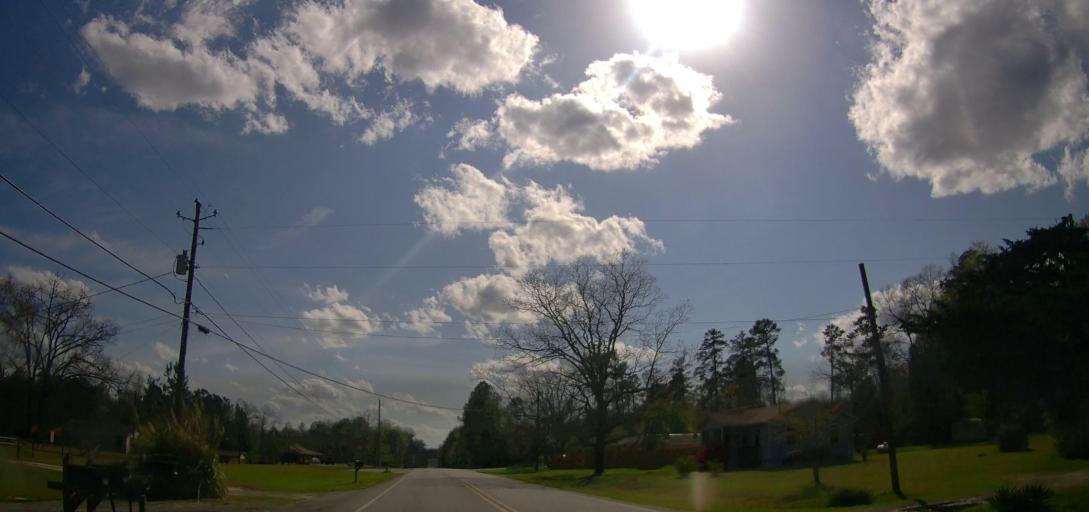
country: US
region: Georgia
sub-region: Wilkinson County
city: Gordon
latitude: 32.9737
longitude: -83.2822
